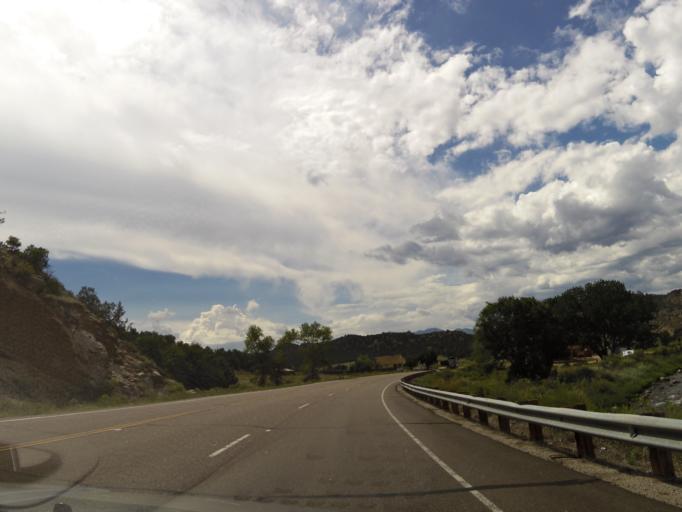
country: US
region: Colorado
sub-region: Custer County
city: Westcliffe
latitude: 38.3930
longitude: -105.6220
